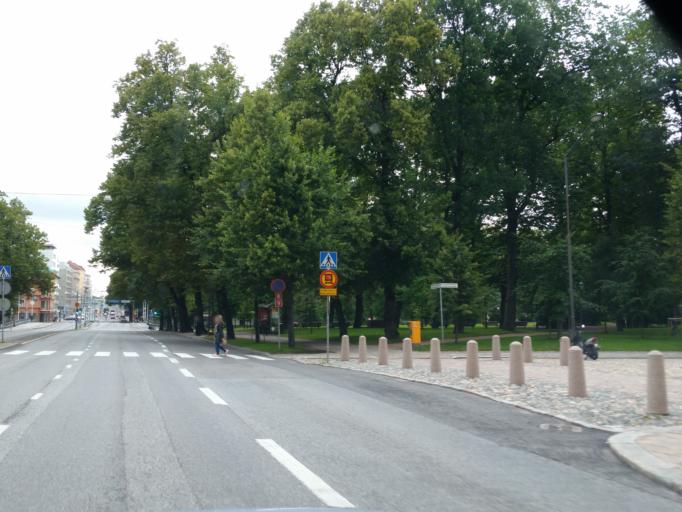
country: FI
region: Varsinais-Suomi
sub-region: Turku
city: Turku
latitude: 60.4509
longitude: 22.2771
